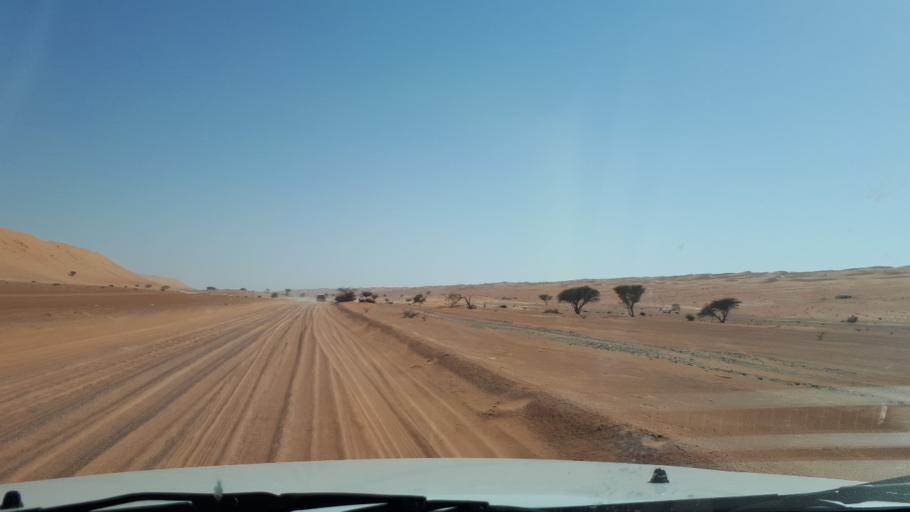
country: OM
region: Ash Sharqiyah
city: Badiyah
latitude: 22.4499
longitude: 58.7368
